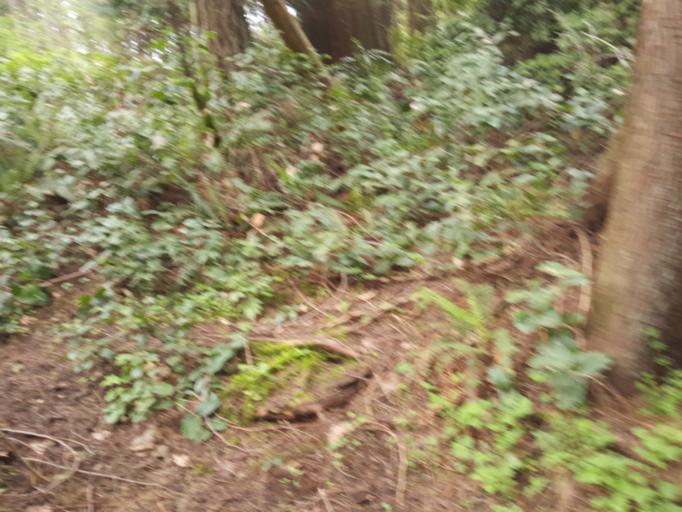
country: US
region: Washington
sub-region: Pierce County
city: University Place
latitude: 47.2050
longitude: -122.5389
